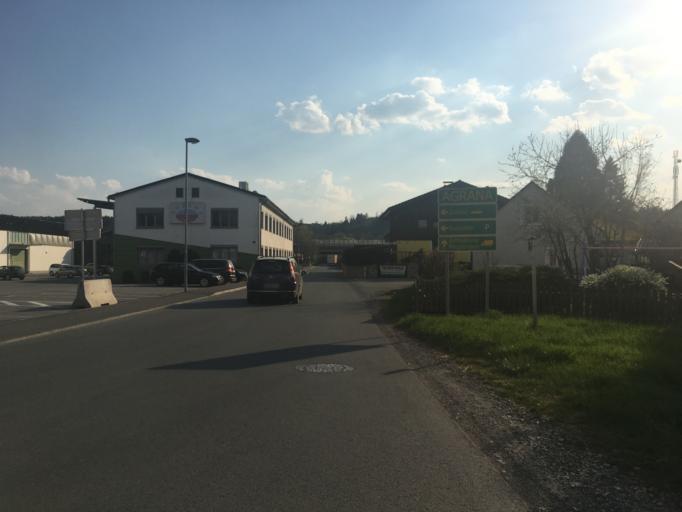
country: AT
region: Styria
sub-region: Politischer Bezirk Weiz
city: Gleisdorf
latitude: 47.1015
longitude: 15.7034
